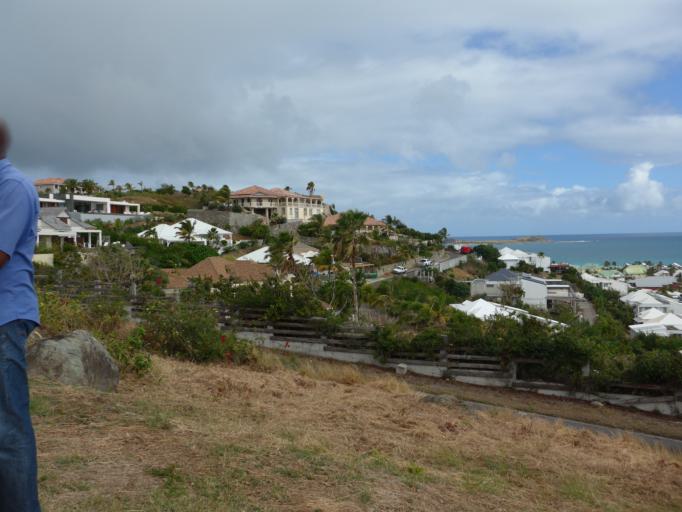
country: MF
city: Marigot
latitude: 18.0843
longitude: -63.0253
